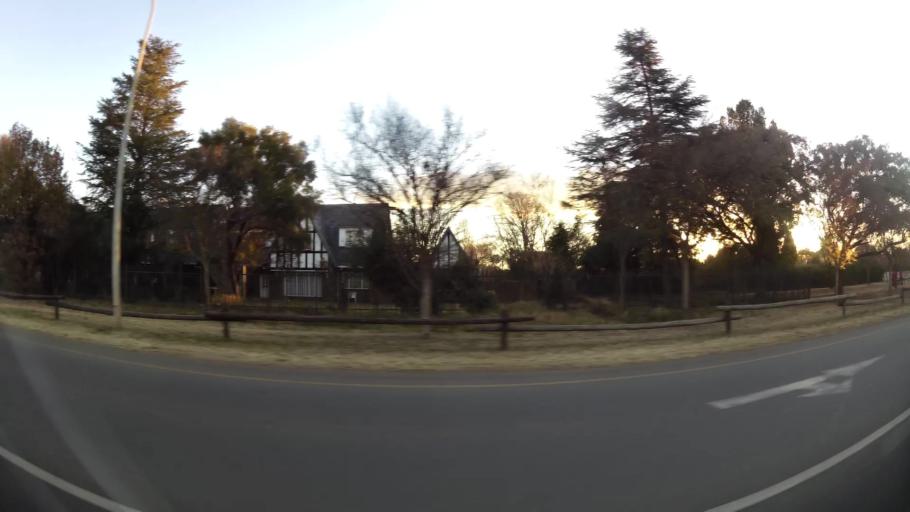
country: ZA
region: North-West
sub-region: Dr Kenneth Kaunda District Municipality
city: Potchefstroom
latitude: -26.7205
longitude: 27.1147
